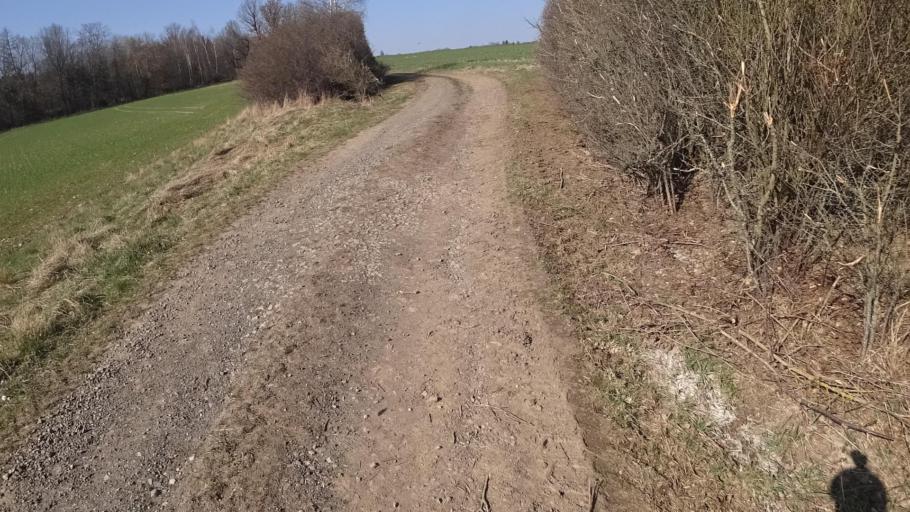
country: DE
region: Rheinland-Pfalz
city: Rheinbollen
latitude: 50.0185
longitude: 7.6616
